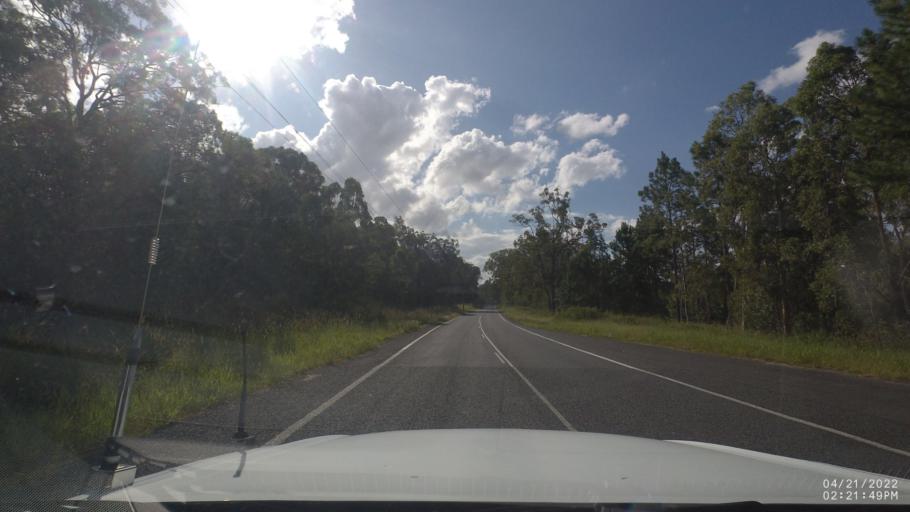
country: AU
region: Queensland
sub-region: Logan
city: Chambers Flat
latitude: -27.8320
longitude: 153.1063
